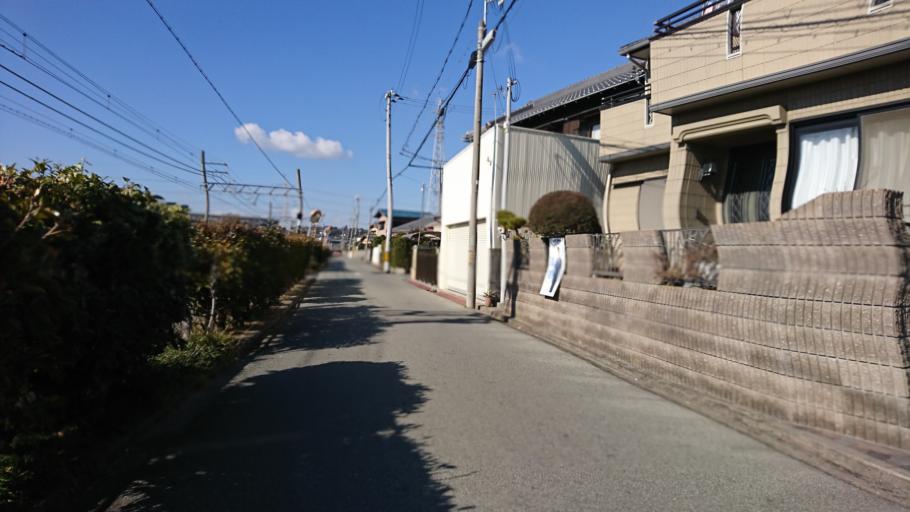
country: JP
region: Hyogo
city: Kakogawacho-honmachi
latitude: 34.7712
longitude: 134.7831
